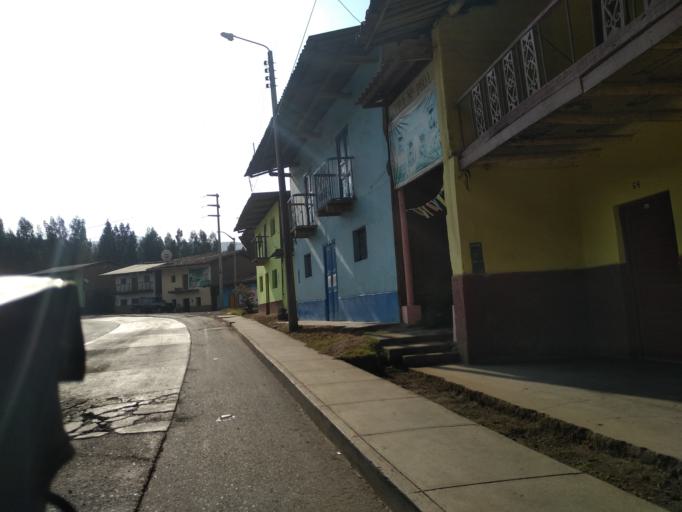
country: PE
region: La Libertad
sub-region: Provincia de Otuzco
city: Agallpampa
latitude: -7.9945
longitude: -78.5207
